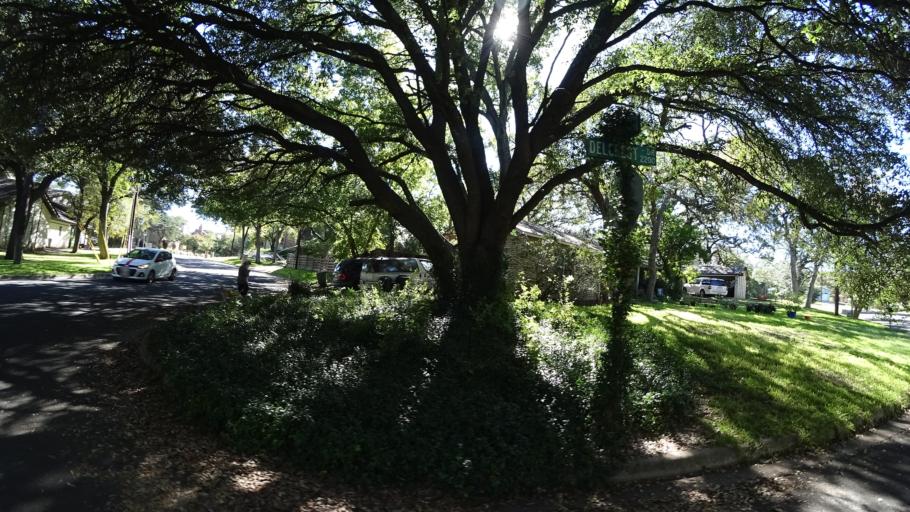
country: US
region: Texas
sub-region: Travis County
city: Rollingwood
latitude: 30.2455
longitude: -97.7742
